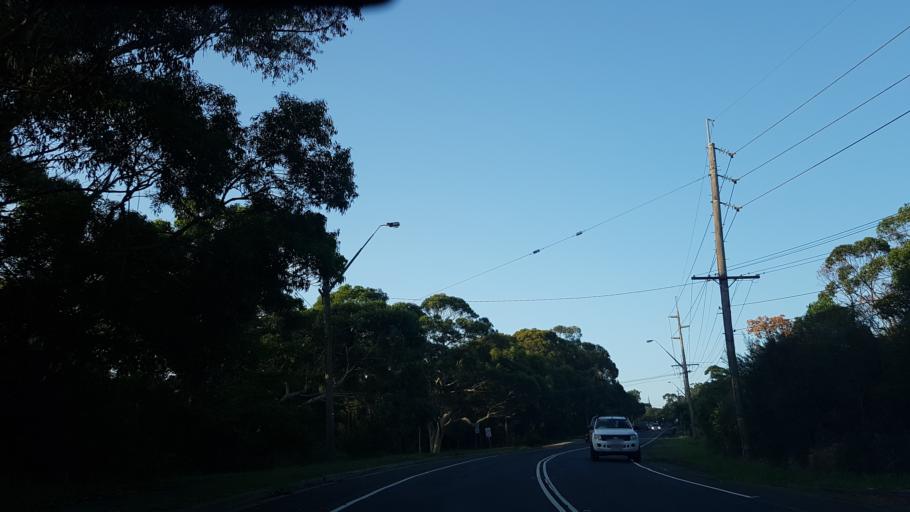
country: AU
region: New South Wales
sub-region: Warringah
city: Narraweena
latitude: -33.7458
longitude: 151.2645
